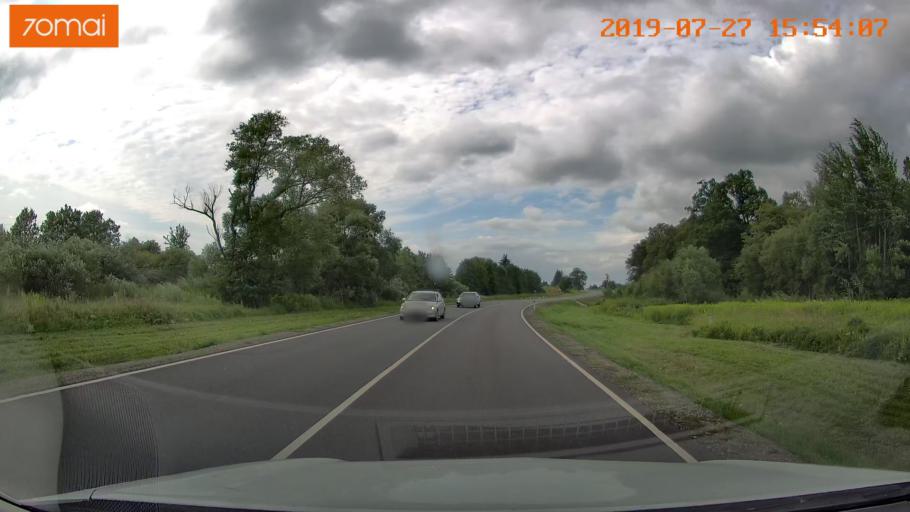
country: RU
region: Kaliningrad
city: Chernyakhovsk
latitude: 54.6059
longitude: 21.9434
